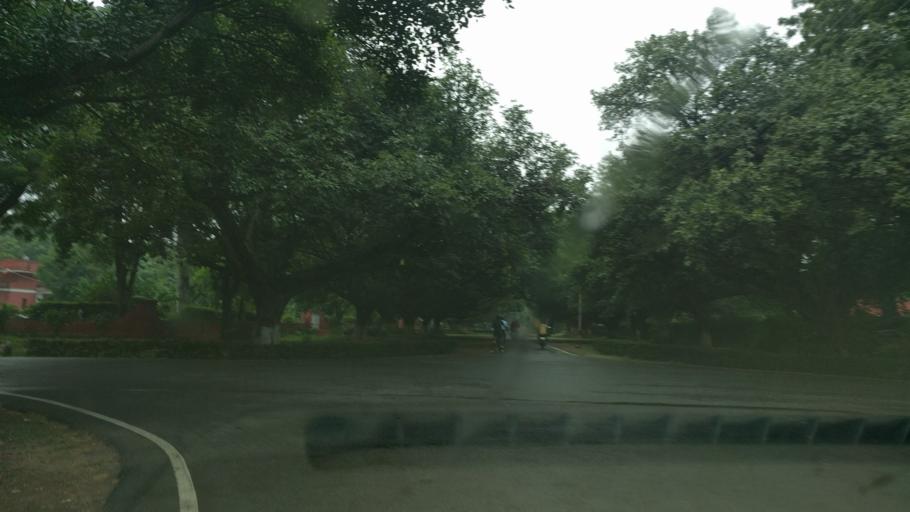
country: IN
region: NCT
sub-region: Central Delhi
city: Karol Bagh
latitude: 28.6378
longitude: 77.1647
